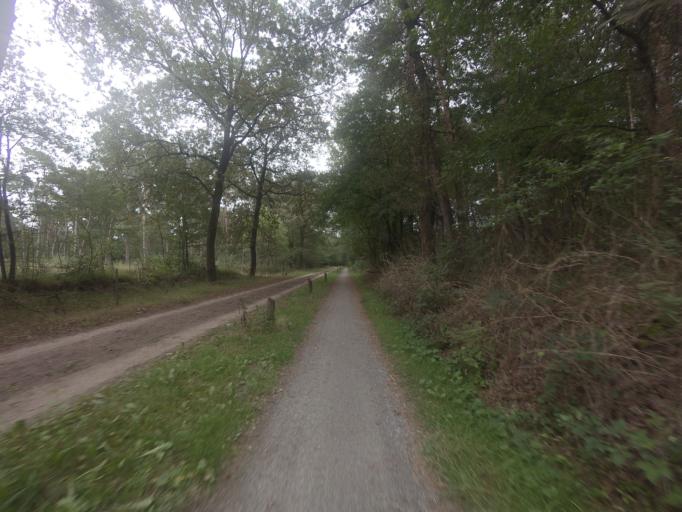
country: NL
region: Drenthe
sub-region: Gemeente Westerveld
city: Dwingeloo
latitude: 52.8797
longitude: 6.2692
